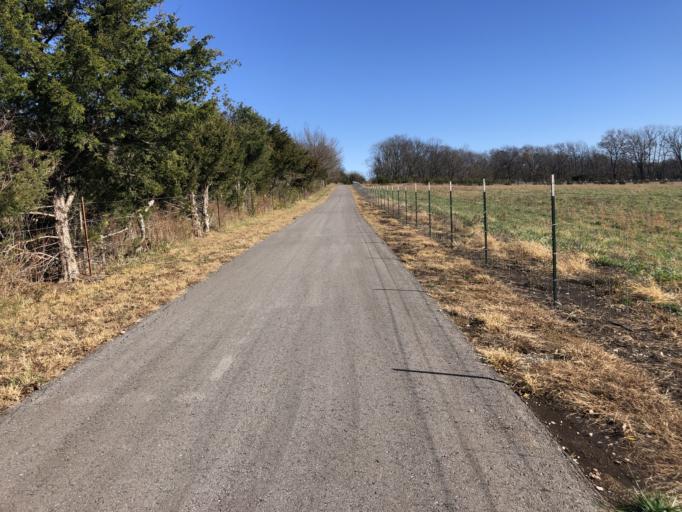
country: US
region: Kansas
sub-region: Johnson County
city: Gardner
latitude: 38.8766
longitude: -94.9570
